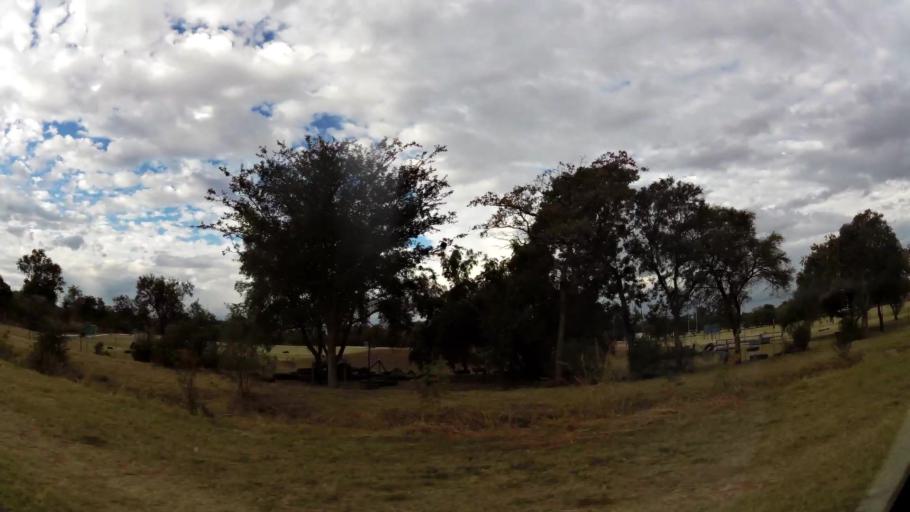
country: ZA
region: Limpopo
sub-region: Waterberg District Municipality
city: Modimolle
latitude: -24.5102
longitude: 28.7053
